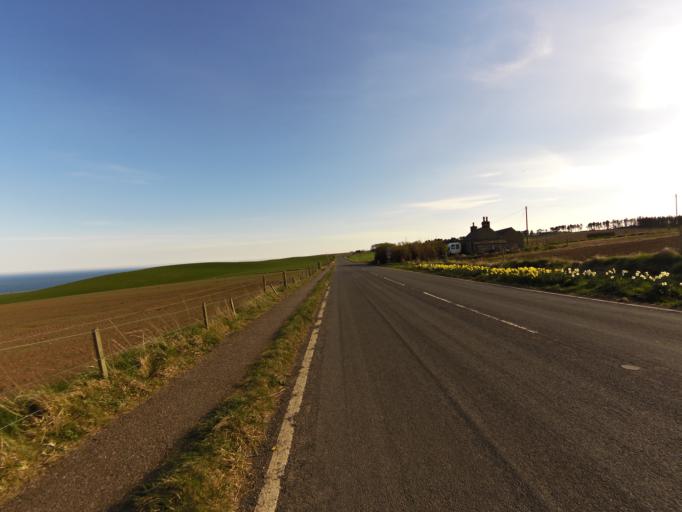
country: GB
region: Scotland
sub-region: Aberdeenshire
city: Stonehaven
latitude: 56.9528
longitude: -2.2053
